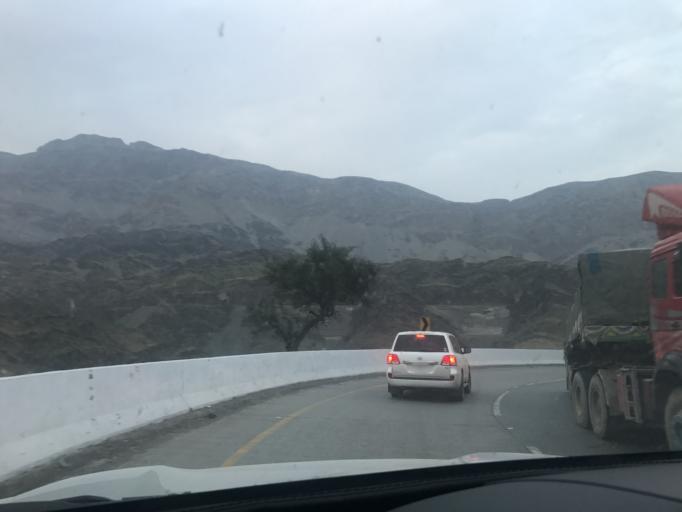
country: PK
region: Federally Administered Tribal Areas
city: Landi Kotal
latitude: 34.0098
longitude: 71.2952
